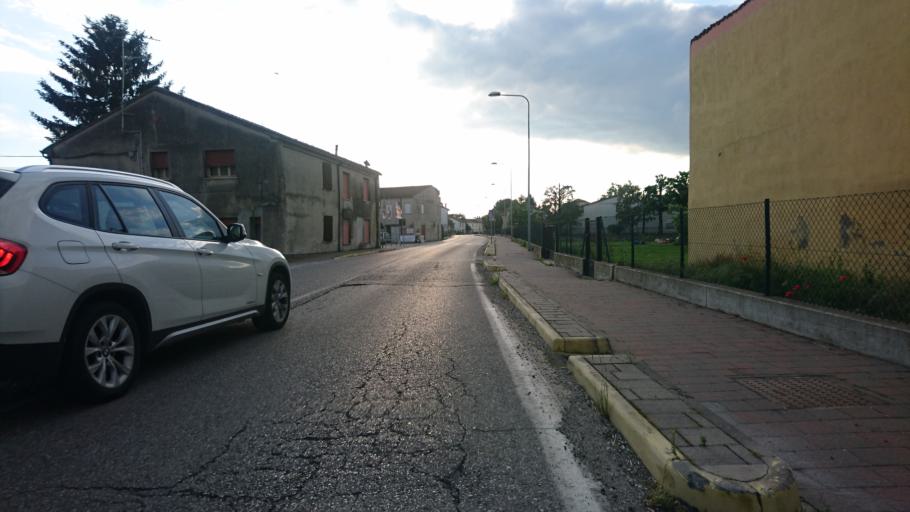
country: IT
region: Veneto
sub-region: Provincia di Rovigo
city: Ceneselli
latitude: 45.0146
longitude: 11.3686
